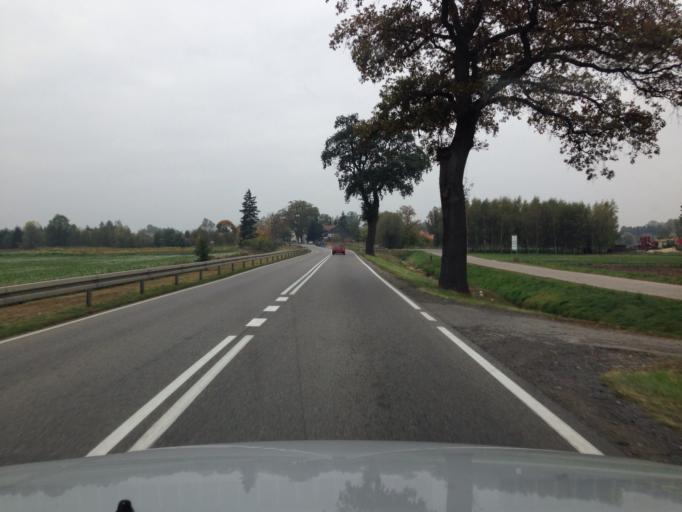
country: PL
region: Warmian-Masurian Voivodeship
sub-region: Powiat elblaski
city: Gronowo Elblaskie
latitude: 54.1262
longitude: 19.3084
